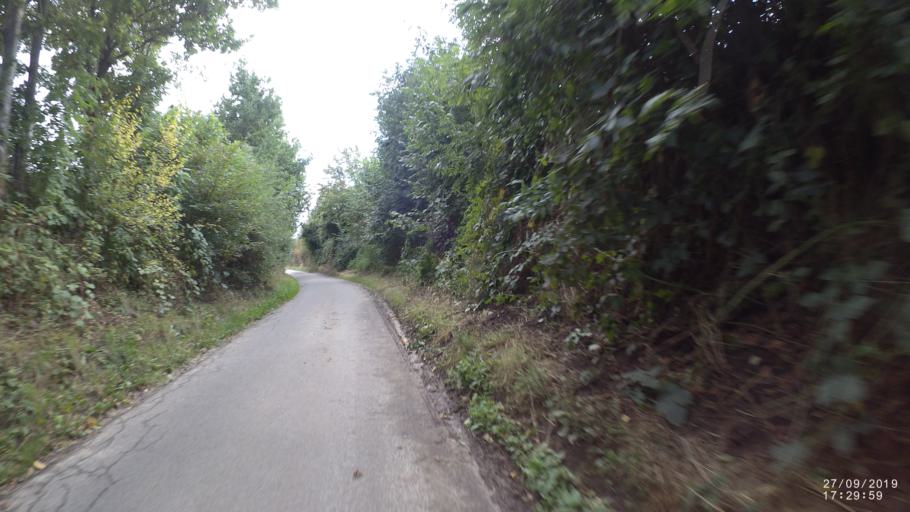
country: BE
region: Flanders
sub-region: Provincie Oost-Vlaanderen
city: Zottegem
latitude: 50.8487
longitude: 3.7868
